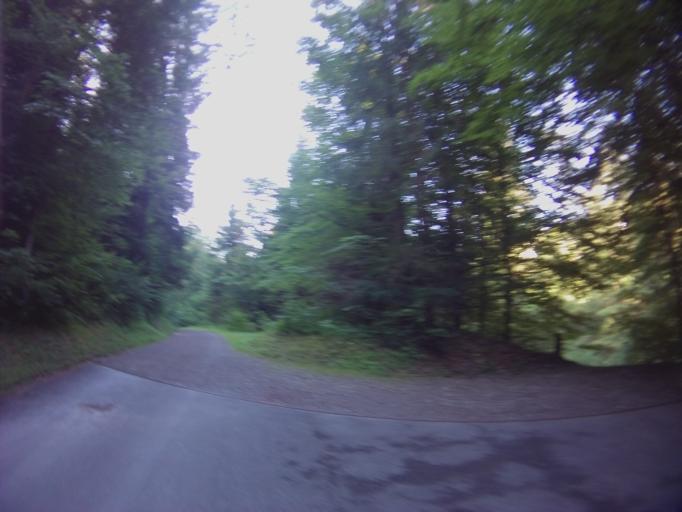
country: CH
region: Zug
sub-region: Zug
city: Menzingen
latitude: 47.1620
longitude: 8.5616
